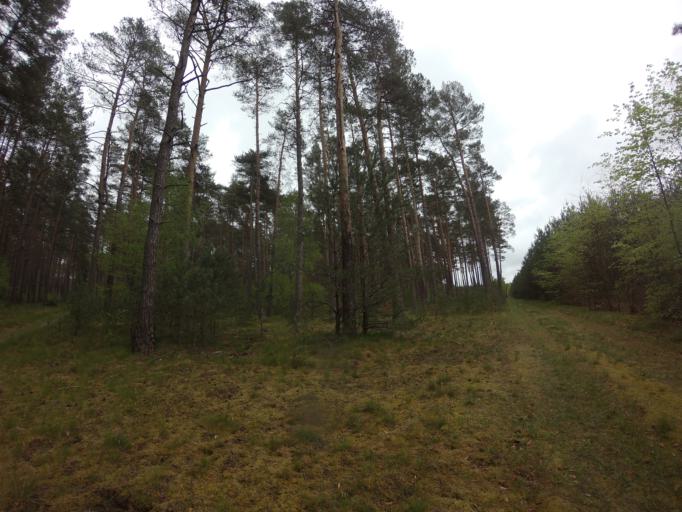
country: PL
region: West Pomeranian Voivodeship
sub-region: Powiat drawski
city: Kalisz Pomorski
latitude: 53.2191
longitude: 16.0079
